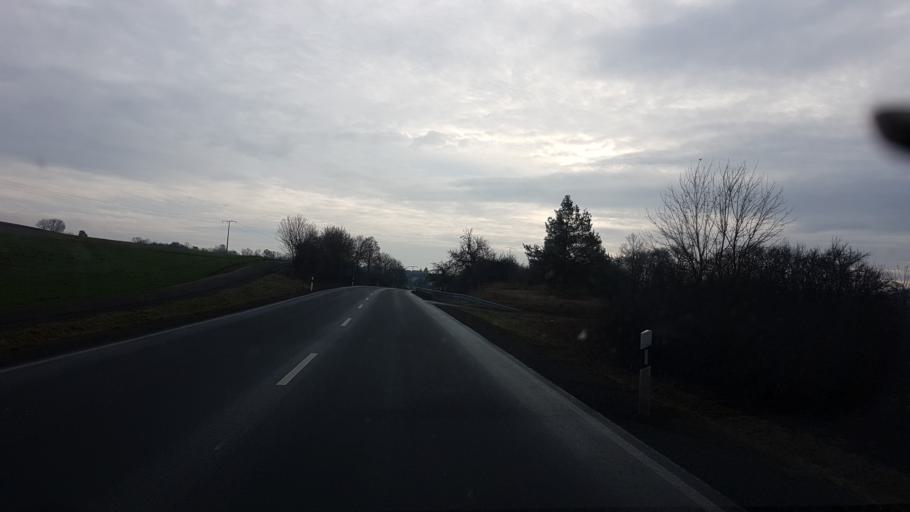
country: DE
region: Bavaria
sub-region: Regierungsbezirk Unterfranken
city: Pfarrweisach
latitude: 50.1525
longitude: 10.7372
